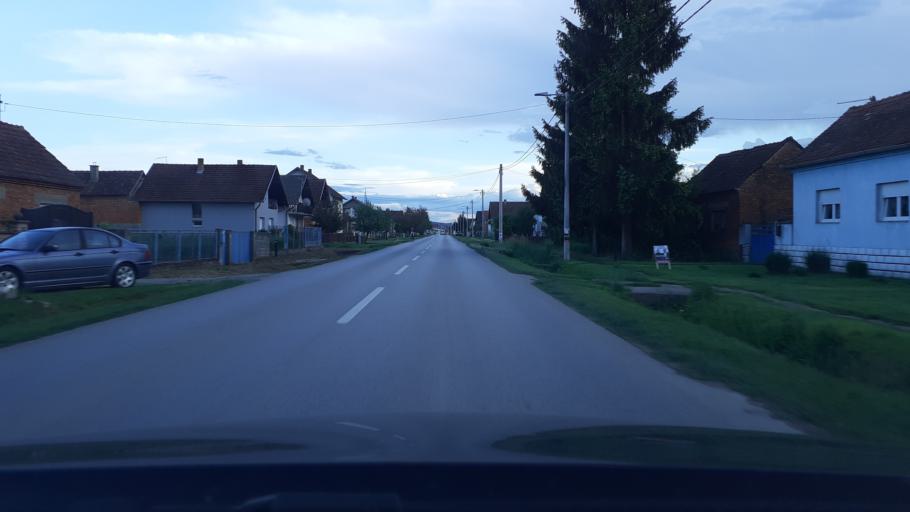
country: HR
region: Pozesko-Slavonska
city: Pleternica
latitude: 45.3018
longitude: 17.8079
